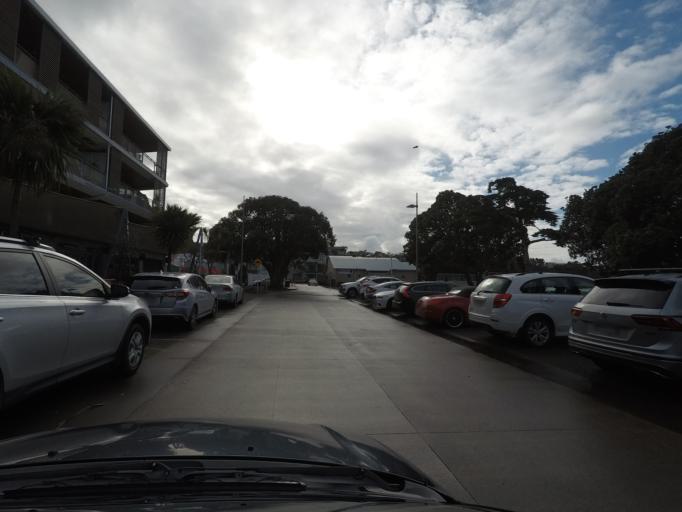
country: NZ
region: Auckland
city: Murrays Bay
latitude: -36.7140
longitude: 174.7490
